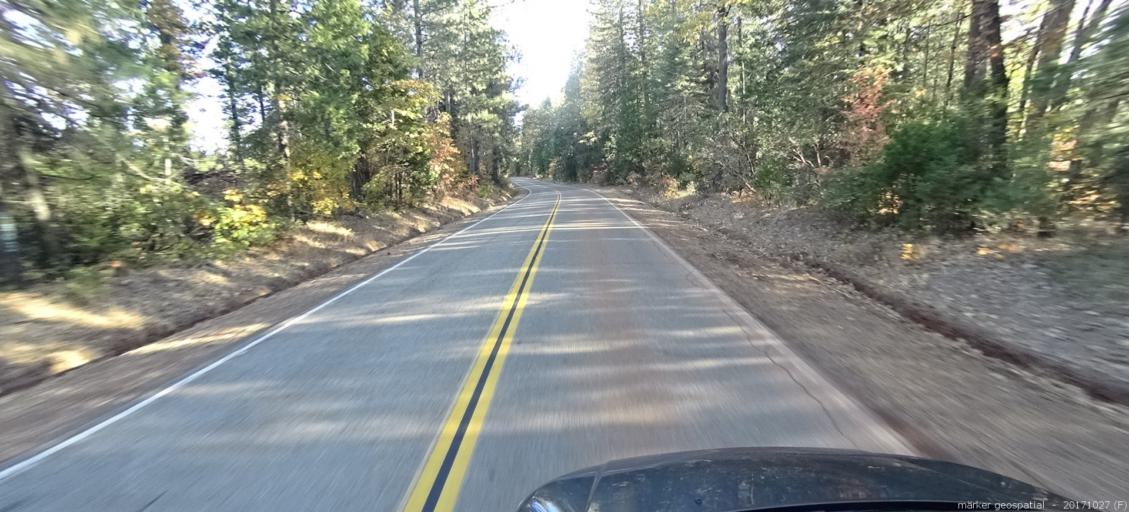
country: US
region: California
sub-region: Shasta County
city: Burney
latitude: 40.9618
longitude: -121.9407
